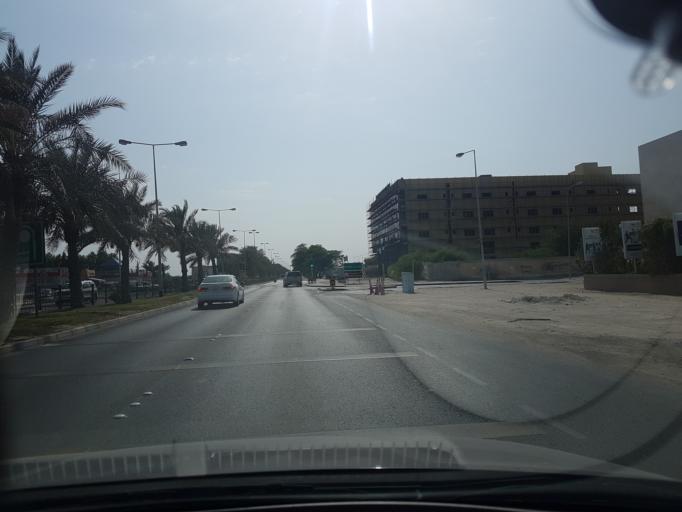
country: BH
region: Manama
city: Jidd Hafs
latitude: 26.2185
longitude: 50.4867
